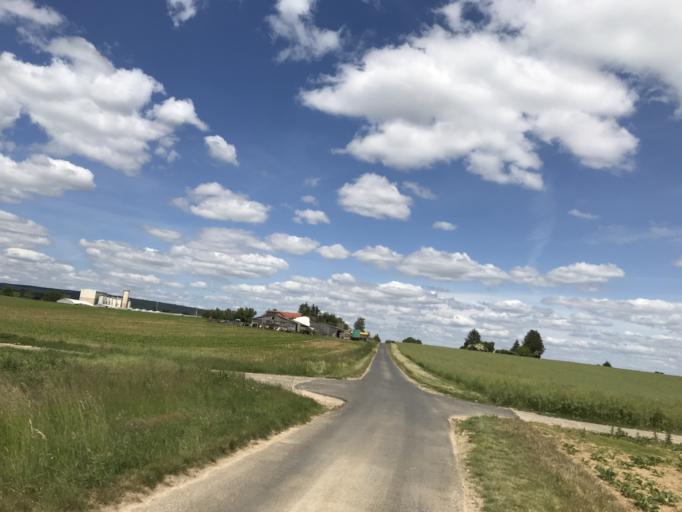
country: DE
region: Hesse
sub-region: Regierungsbezirk Darmstadt
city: Ober-Morlen
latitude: 50.3960
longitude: 8.6728
